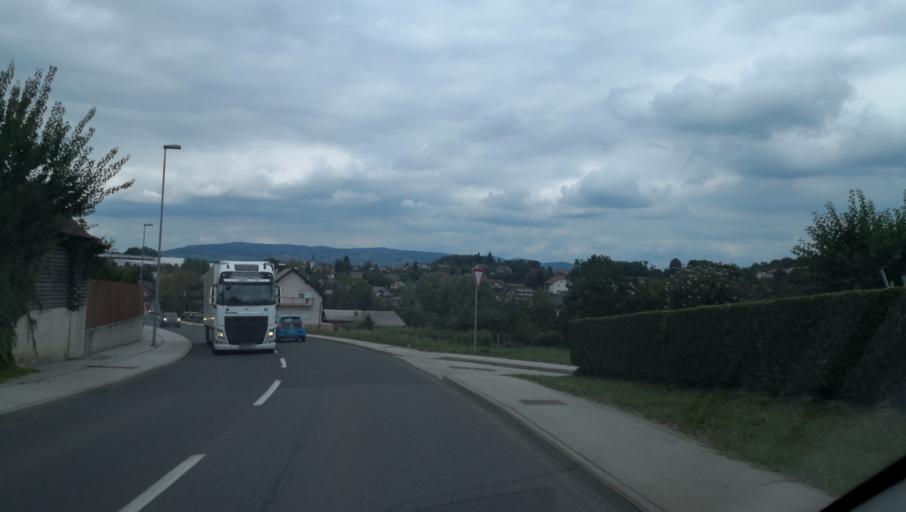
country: SI
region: Novo Mesto
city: Novo Mesto
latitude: 45.7850
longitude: 15.1804
